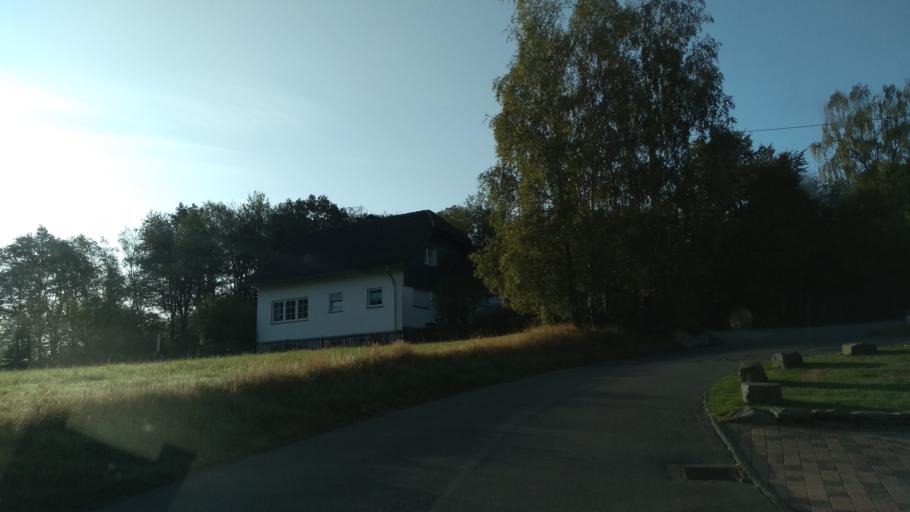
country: DE
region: North Rhine-Westphalia
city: Kierspe
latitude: 51.0909
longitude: 7.5990
